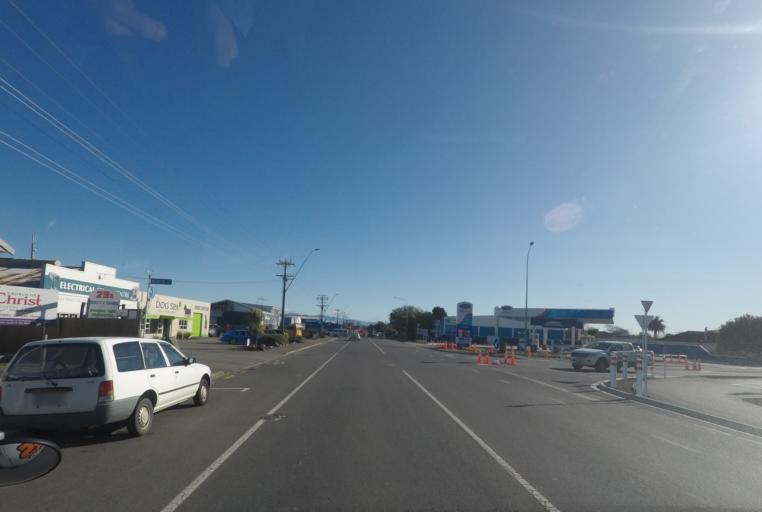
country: NZ
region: Nelson
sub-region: Nelson City
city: Nelson
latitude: -41.2911
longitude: 173.2437
